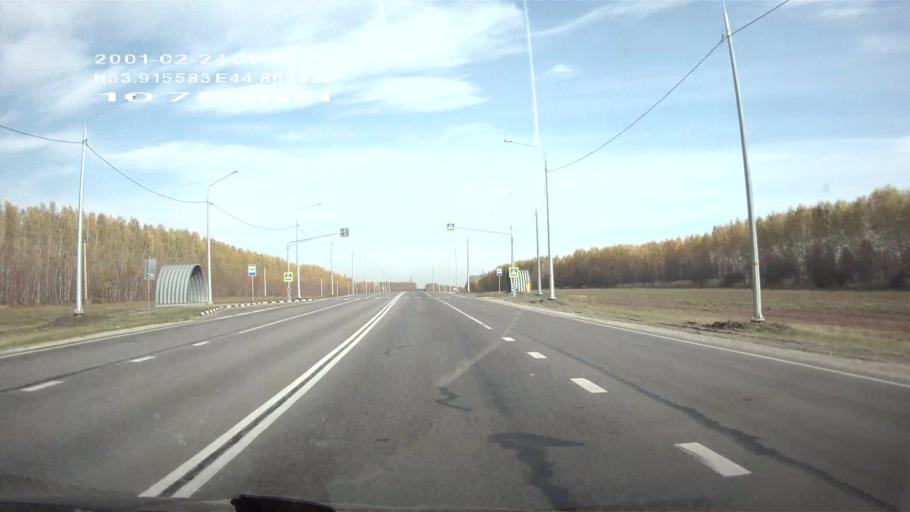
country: RU
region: Penza
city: Issa
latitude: 53.9160
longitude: 44.8644
